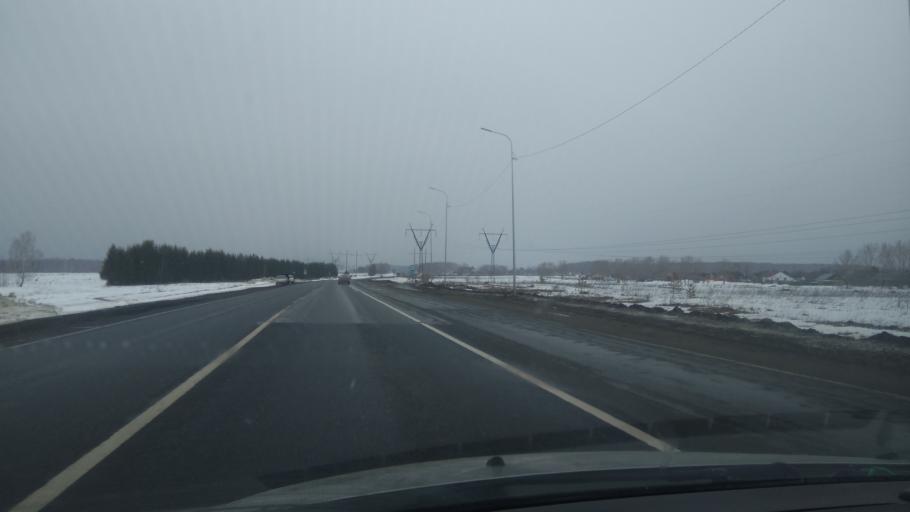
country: RU
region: Perm
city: Orda
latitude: 57.2571
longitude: 57.0308
